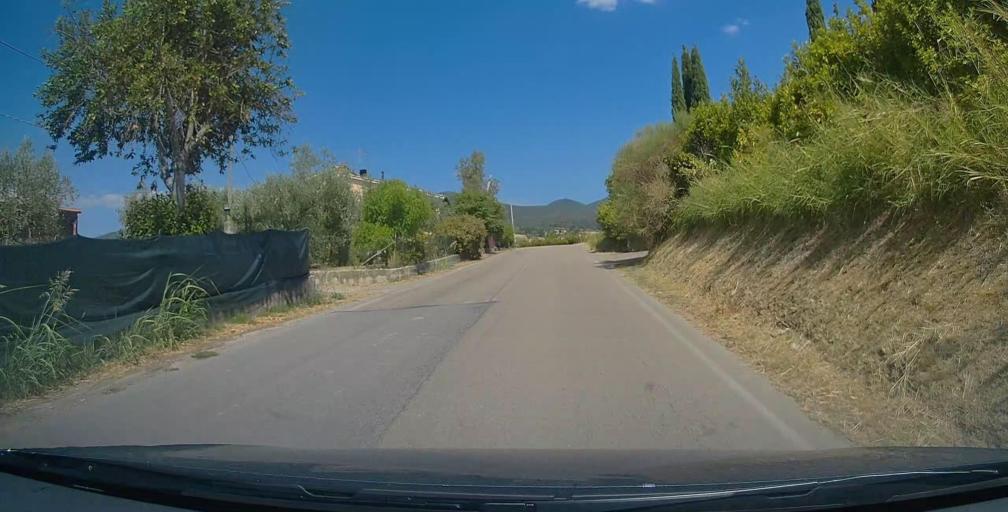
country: IT
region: Umbria
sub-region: Provincia di Terni
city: Calvi dell'Umbria
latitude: 42.4107
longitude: 12.5296
